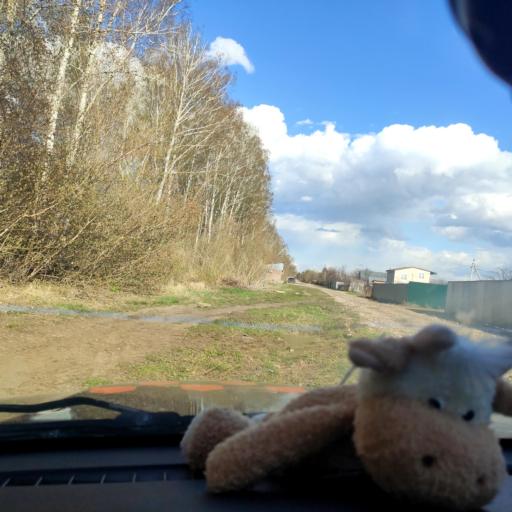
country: RU
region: Samara
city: Tol'yatti
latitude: 53.5986
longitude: 49.3090
